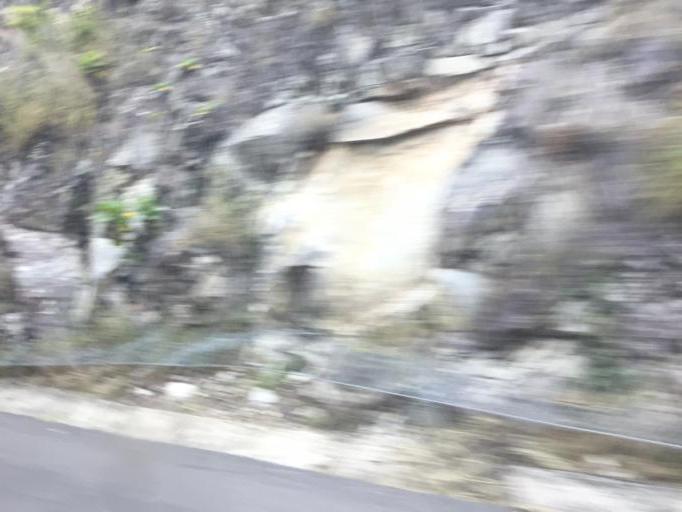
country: MX
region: Jalisco
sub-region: Zapotlan del Rey
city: Zapotlan del Rey
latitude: 20.4972
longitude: -102.9470
